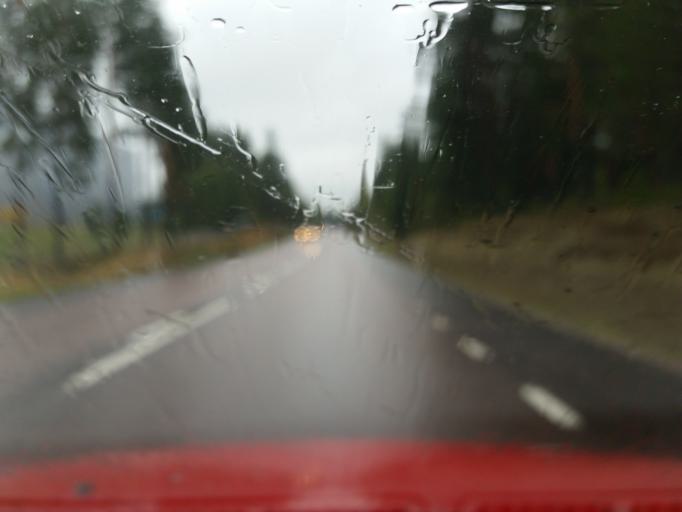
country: SE
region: Dalarna
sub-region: Leksand Municipality
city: Smedby
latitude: 60.6633
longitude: 15.0851
